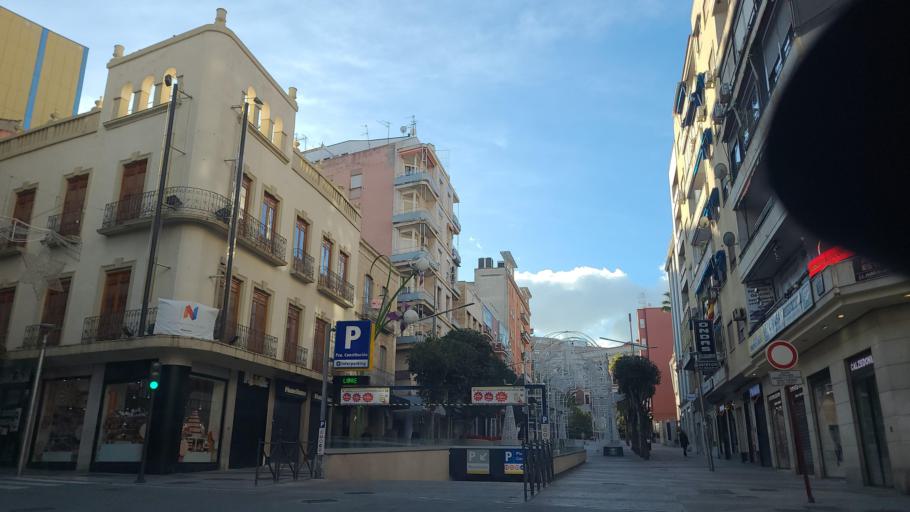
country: ES
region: Andalusia
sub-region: Provincia de Jaen
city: Jaen
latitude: 37.7692
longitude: -3.7883
